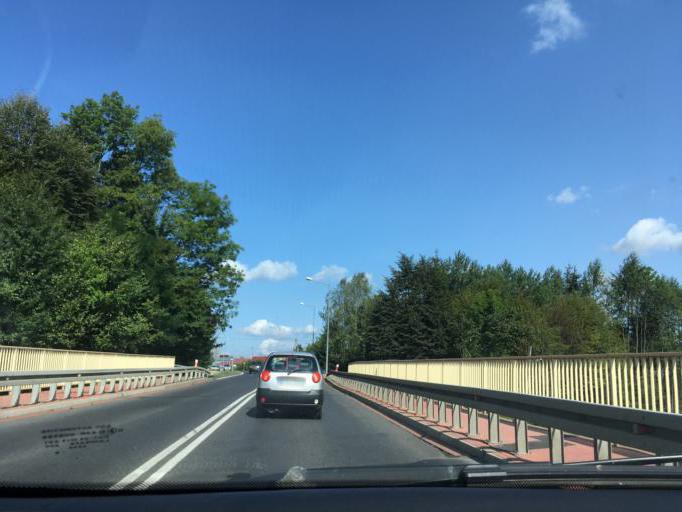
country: PL
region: Subcarpathian Voivodeship
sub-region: Powiat sanocki
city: Zagorz
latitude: 49.5152
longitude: 22.2660
